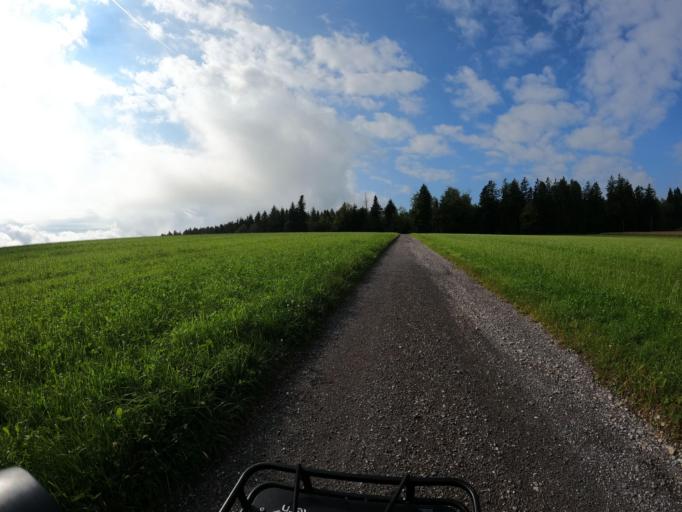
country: CH
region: Aargau
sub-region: Bezirk Muri
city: Buttwil
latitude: 47.2329
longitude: 8.3188
